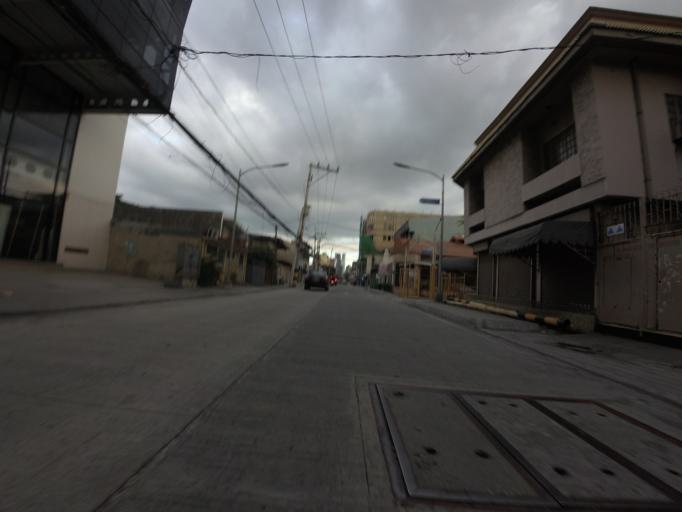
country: PH
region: Metro Manila
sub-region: Makati City
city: Makati City
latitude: 14.5665
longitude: 121.0060
